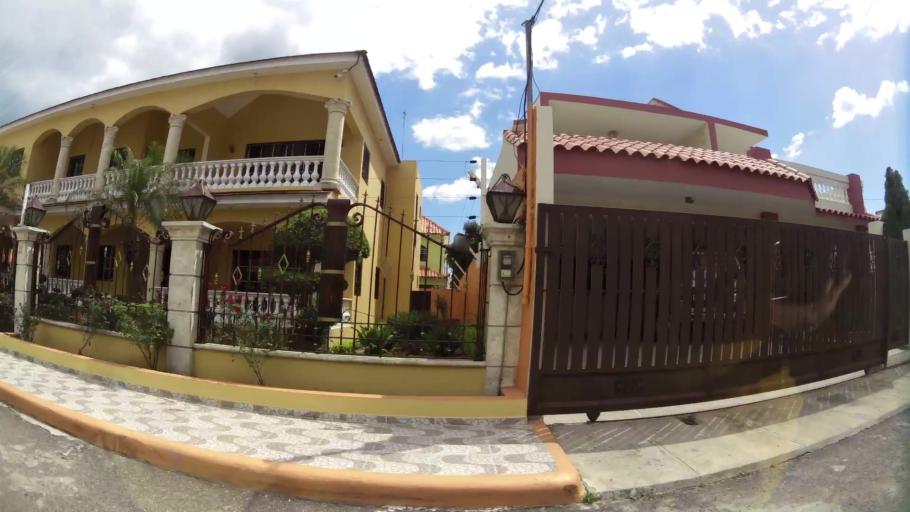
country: DO
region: San Cristobal
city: San Cristobal
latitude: 18.4167
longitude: -70.1022
